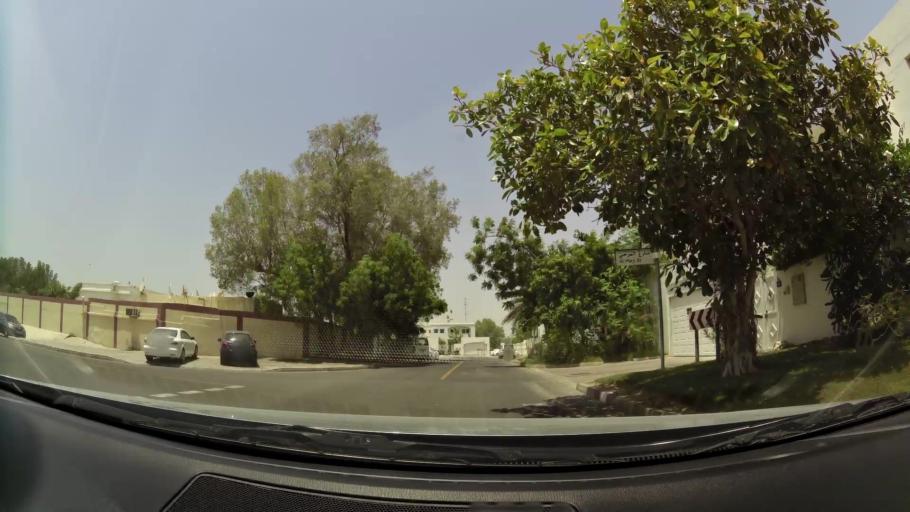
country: AE
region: Dubai
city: Dubai
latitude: 25.1706
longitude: 55.2231
